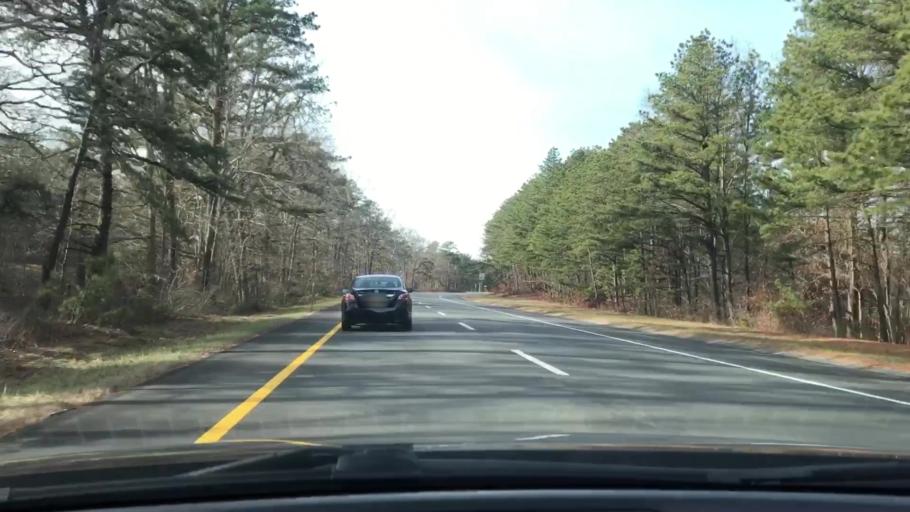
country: US
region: New York
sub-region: Suffolk County
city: Calverton
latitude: 40.9033
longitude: -72.7334
